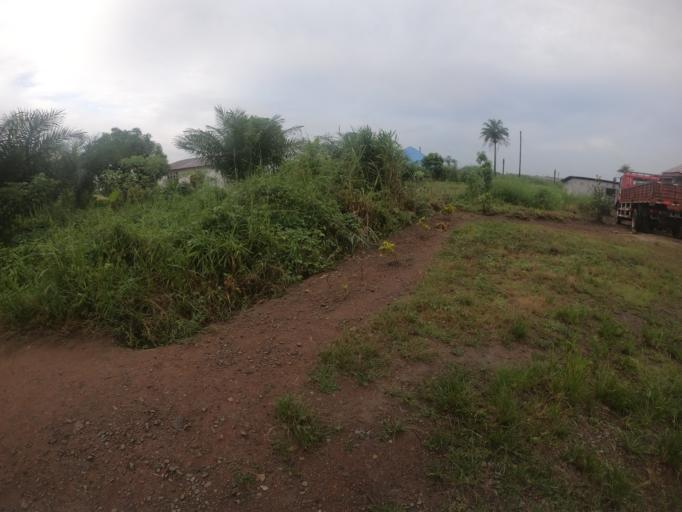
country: SL
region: Southern Province
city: Rotifunk
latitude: 8.4884
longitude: -12.7420
